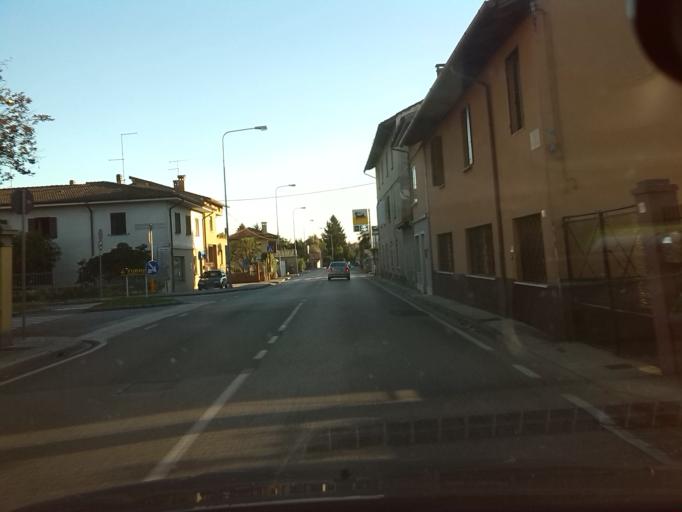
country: IT
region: Friuli Venezia Giulia
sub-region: Provincia di Udine
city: Basaldella
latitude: 46.0427
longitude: 13.2215
